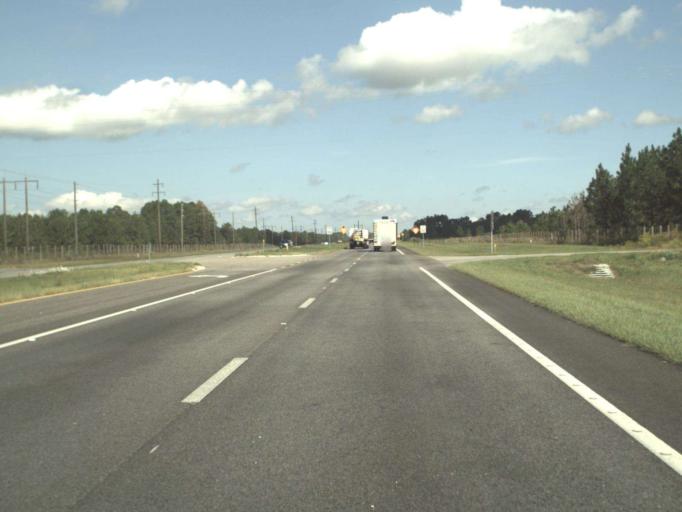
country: US
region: Florida
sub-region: Walton County
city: Freeport
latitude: 30.5736
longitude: -86.1080
